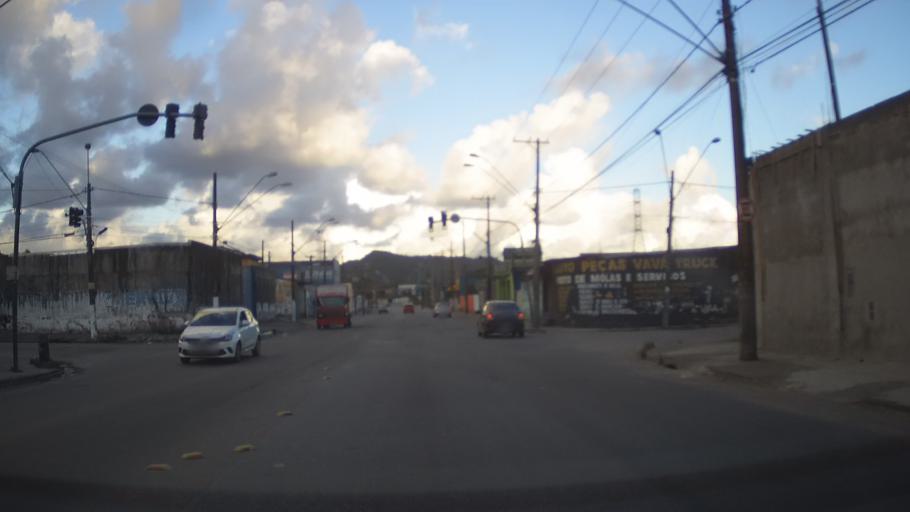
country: BR
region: Sao Paulo
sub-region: Sao Vicente
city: Sao Vicente
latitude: -23.9510
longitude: -46.3947
